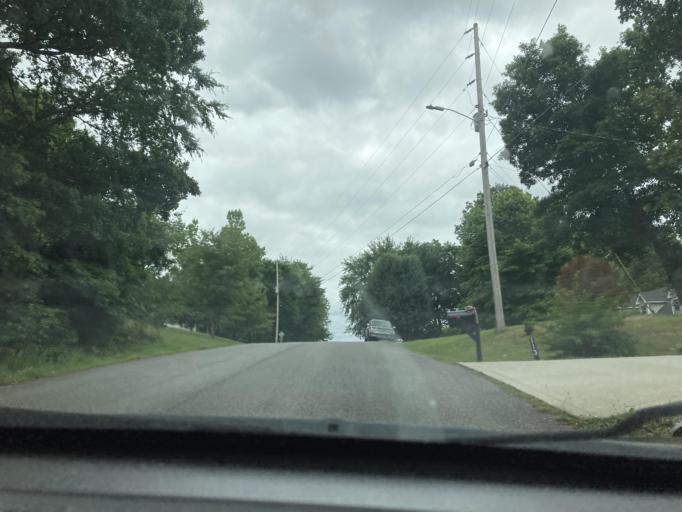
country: US
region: Tennessee
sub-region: Dickson County
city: Dickson
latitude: 36.0997
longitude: -87.3819
